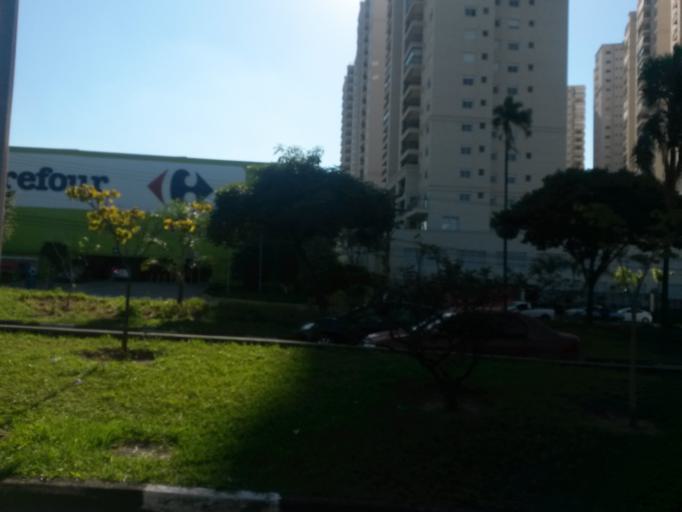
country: BR
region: Sao Paulo
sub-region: Santo Andre
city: Santo Andre
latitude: -23.6701
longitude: -46.5348
